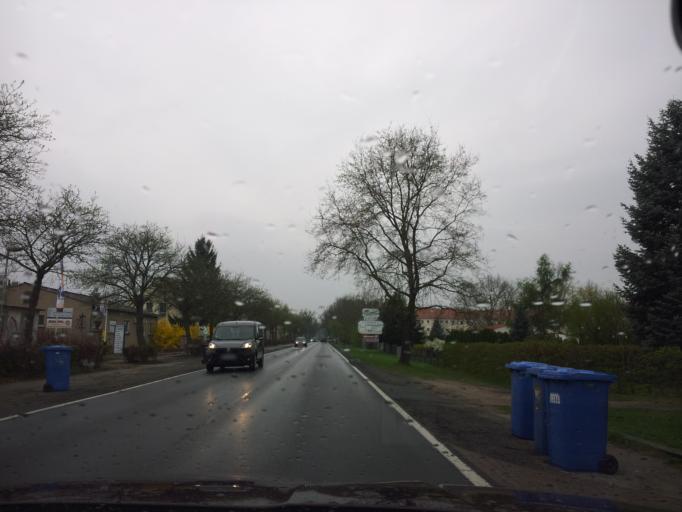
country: DE
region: Brandenburg
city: Treuenbrietzen
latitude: 52.0893
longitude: 12.8541
